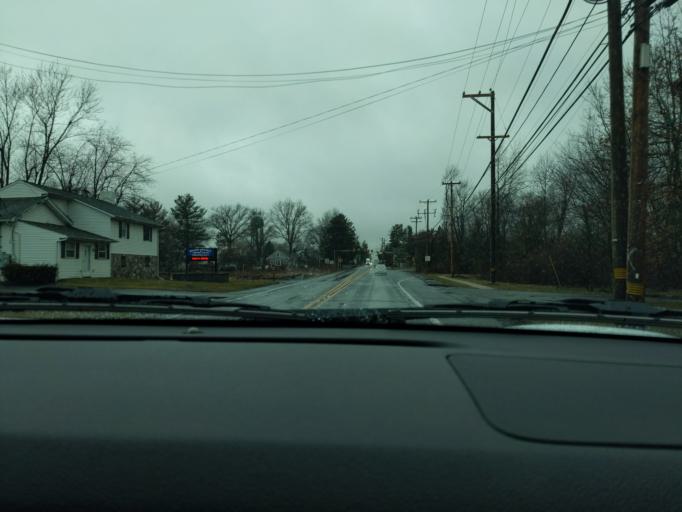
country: US
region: Pennsylvania
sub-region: Bucks County
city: Dublin
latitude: 40.3694
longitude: -75.1994
